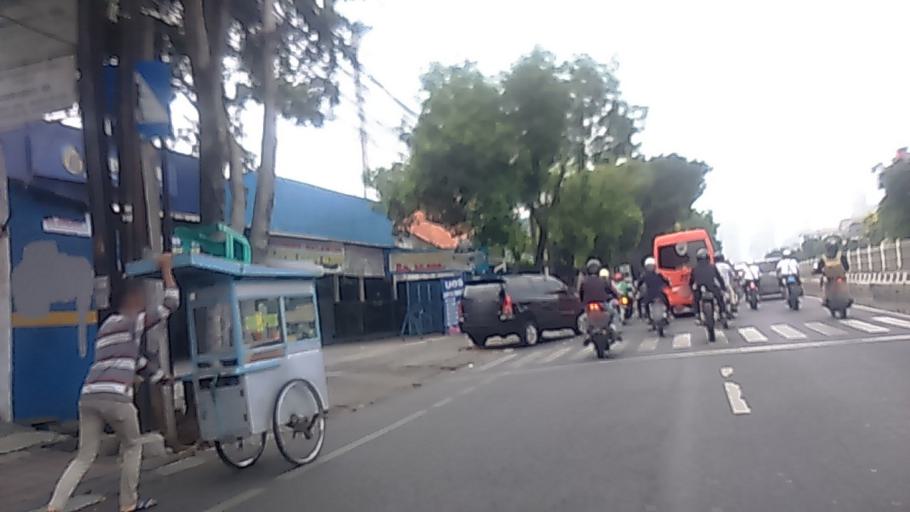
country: ID
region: Jakarta Raya
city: Jakarta
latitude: -6.2518
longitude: 106.8271
